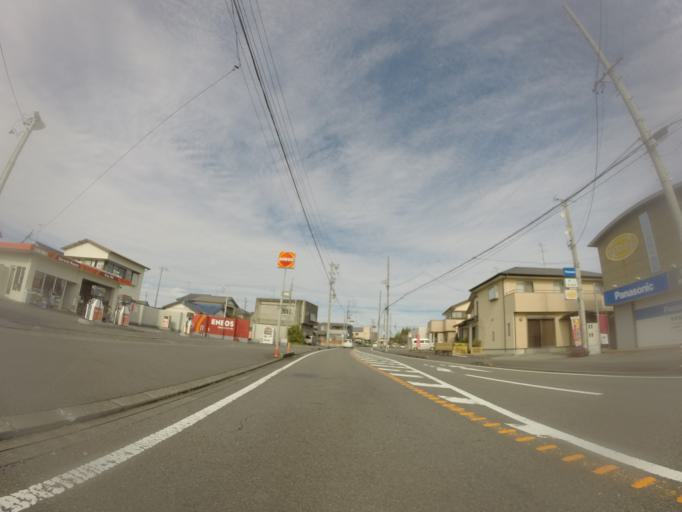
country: JP
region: Shizuoka
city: Shimada
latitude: 34.7867
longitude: 138.2418
